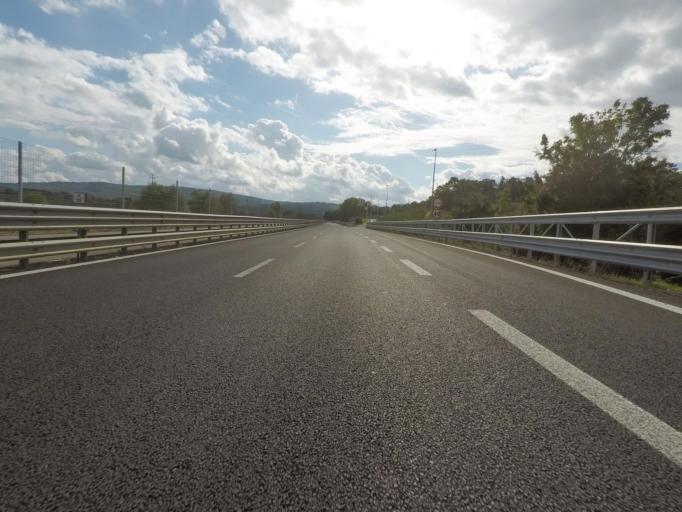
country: IT
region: Tuscany
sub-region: Provincia di Siena
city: Serre di Rapolano
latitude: 43.2565
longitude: 11.6335
